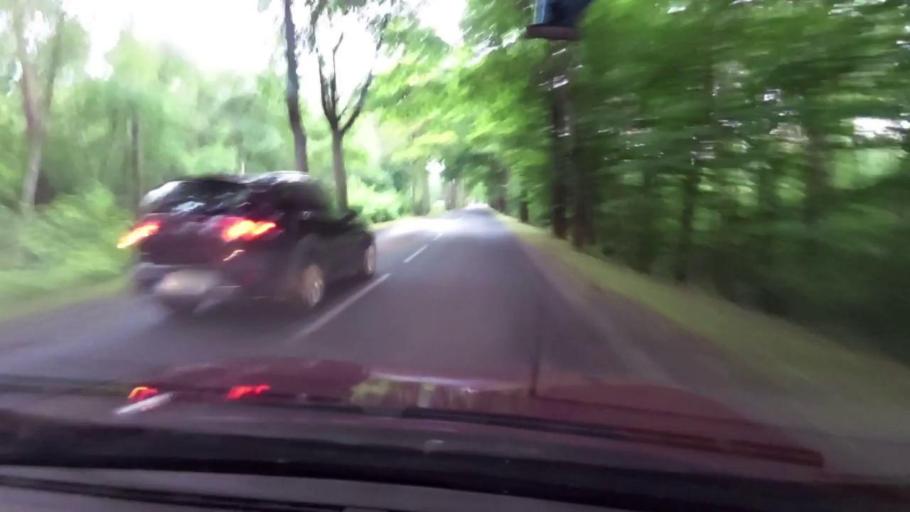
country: PL
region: West Pomeranian Voivodeship
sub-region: Powiat koszalinski
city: Sianow
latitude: 54.1783
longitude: 16.3597
